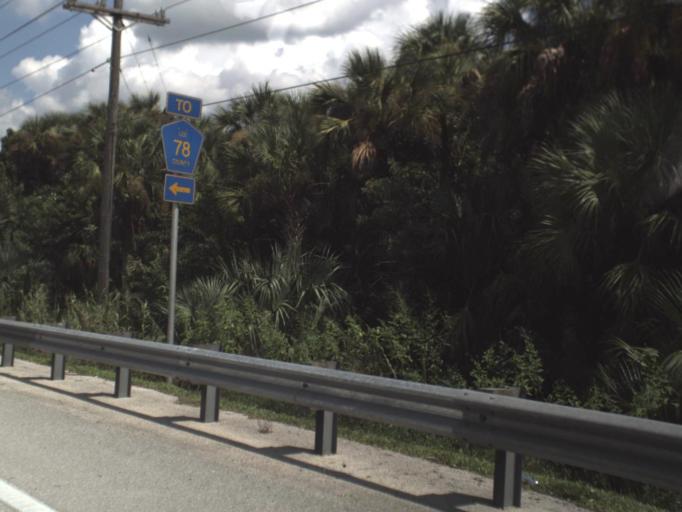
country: US
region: Florida
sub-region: Lee County
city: Fort Myers Shores
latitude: 26.7213
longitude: -81.7619
